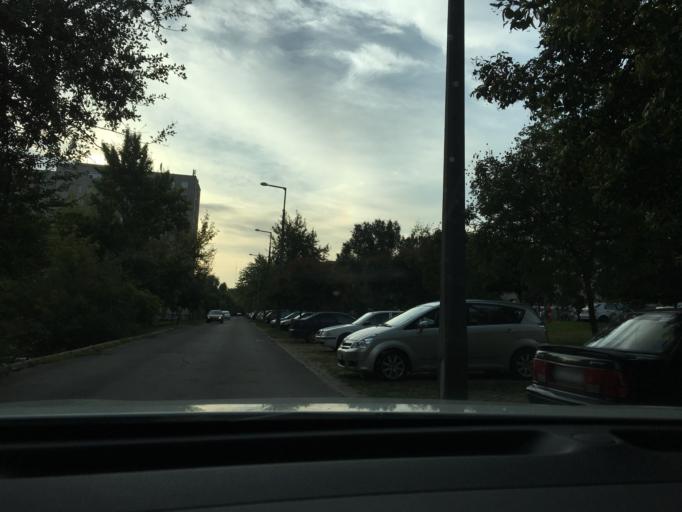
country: HU
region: Budapest
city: Budapest XVII. keruelet
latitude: 47.4804
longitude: 19.2408
